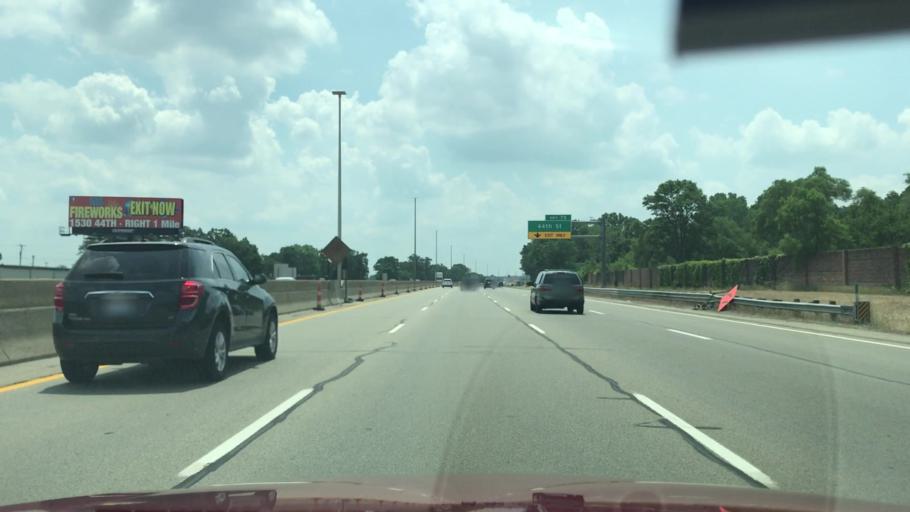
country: US
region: Michigan
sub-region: Kent County
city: Wyoming
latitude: 42.8949
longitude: -85.6784
